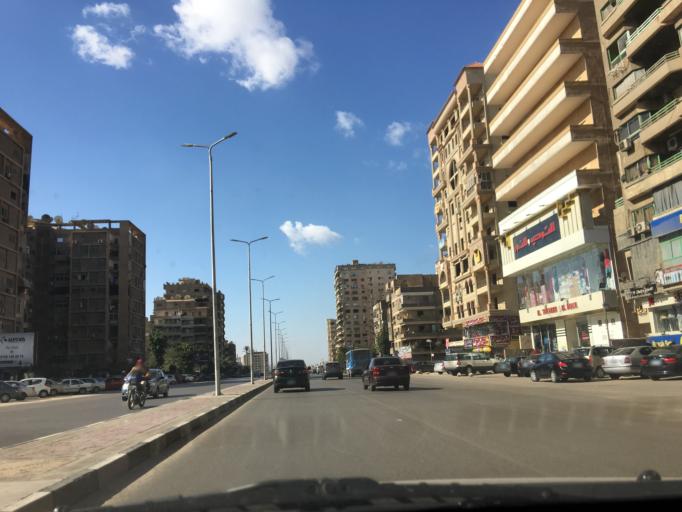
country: EG
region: Muhafazat al Qahirah
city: Cairo
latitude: 30.0532
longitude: 31.3324
